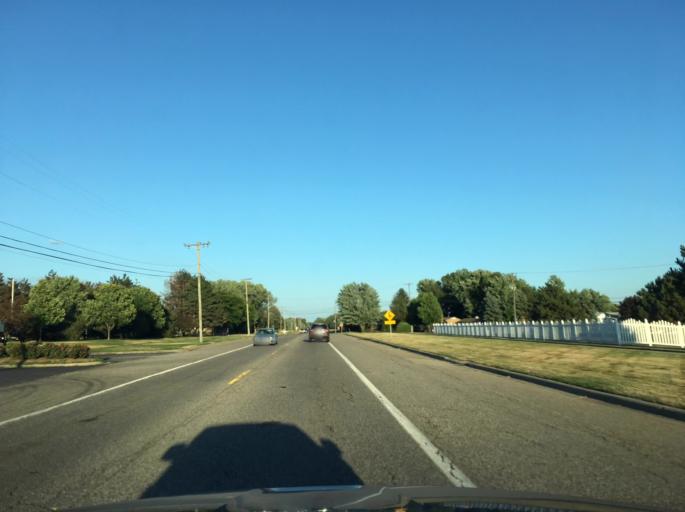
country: US
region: Michigan
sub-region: Macomb County
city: Sterling Heights
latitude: 42.5755
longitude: -82.9854
